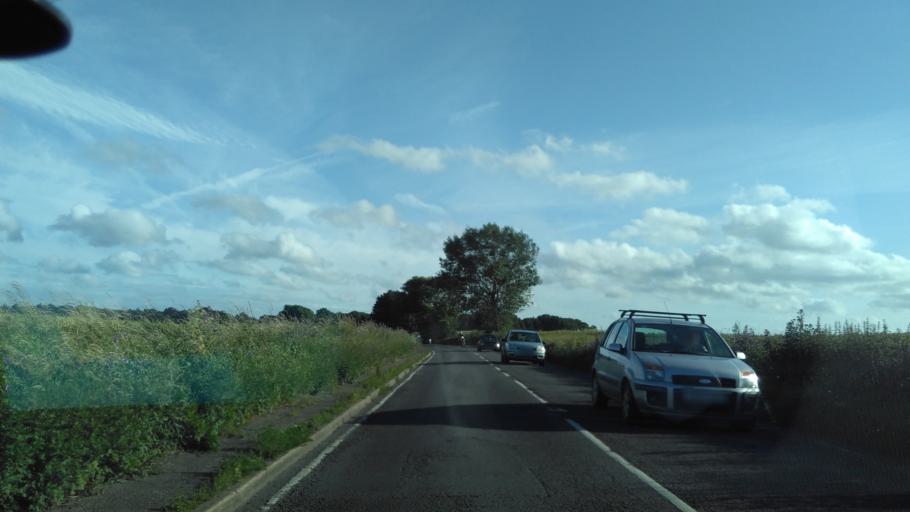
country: GB
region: England
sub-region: Kent
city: Faversham
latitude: 51.2830
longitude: 0.8847
